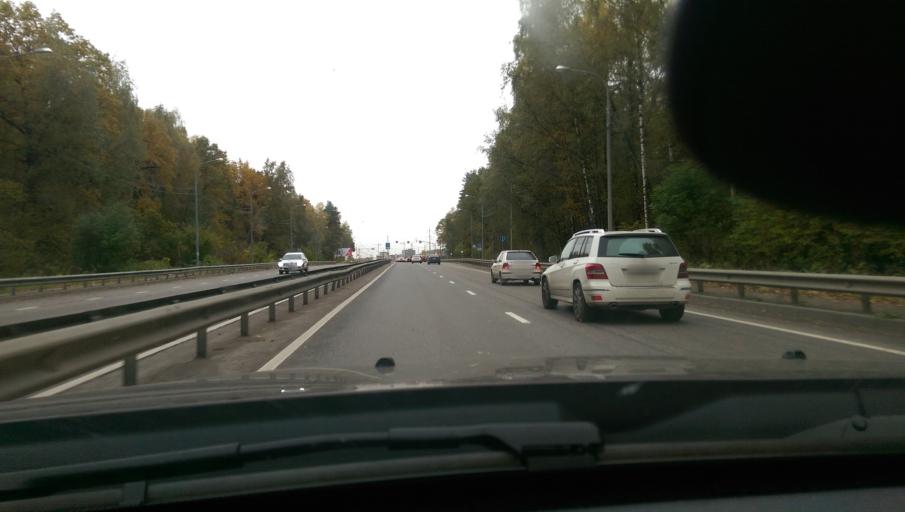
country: RU
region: Moskovskaya
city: Povedniki
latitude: 55.9405
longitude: 37.6552
